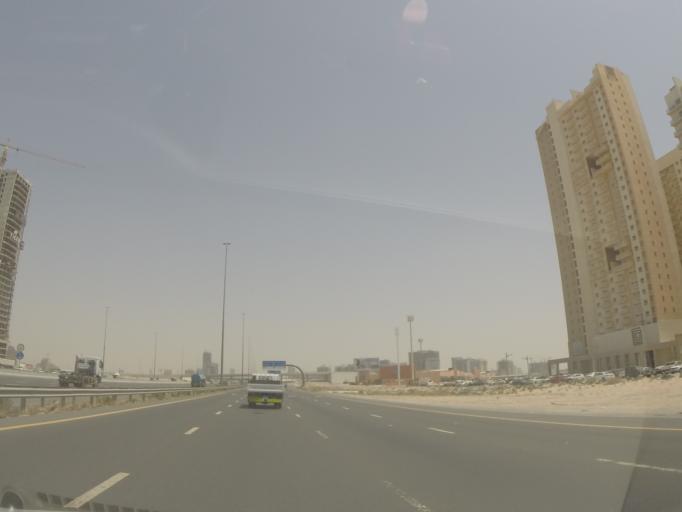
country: AE
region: Dubai
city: Dubai
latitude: 25.0428
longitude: 55.1978
